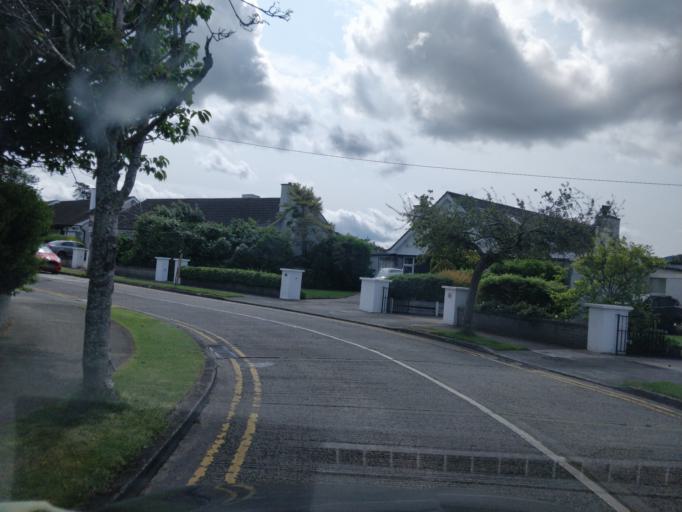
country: IE
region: Leinster
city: Dundrum
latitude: 53.2848
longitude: -6.2476
